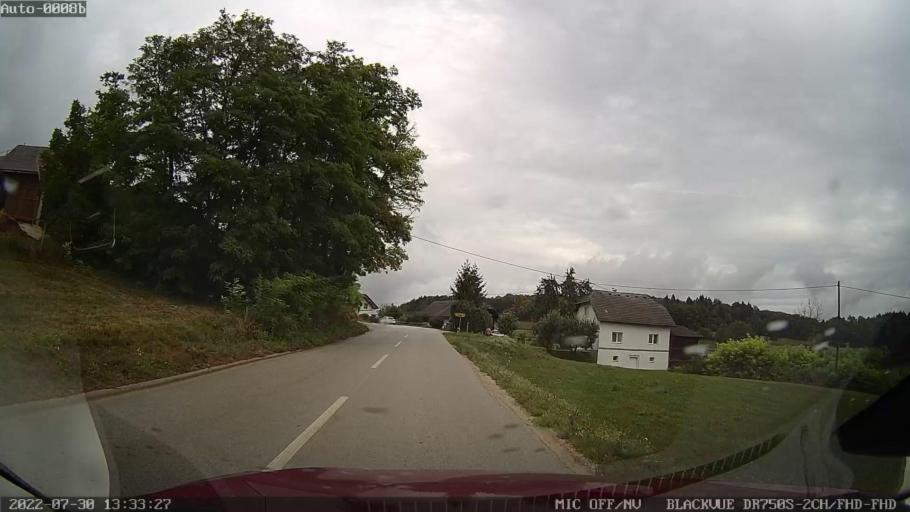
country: SI
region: Zuzemberk
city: Zuzemberk
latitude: 45.8517
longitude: 14.9356
